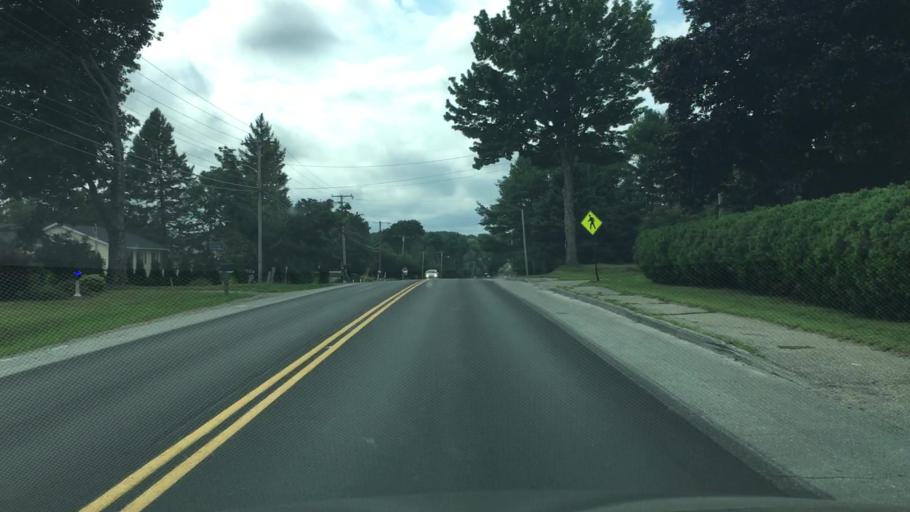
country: US
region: Maine
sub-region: Penobscot County
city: Hampden
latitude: 44.7460
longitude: -68.8560
